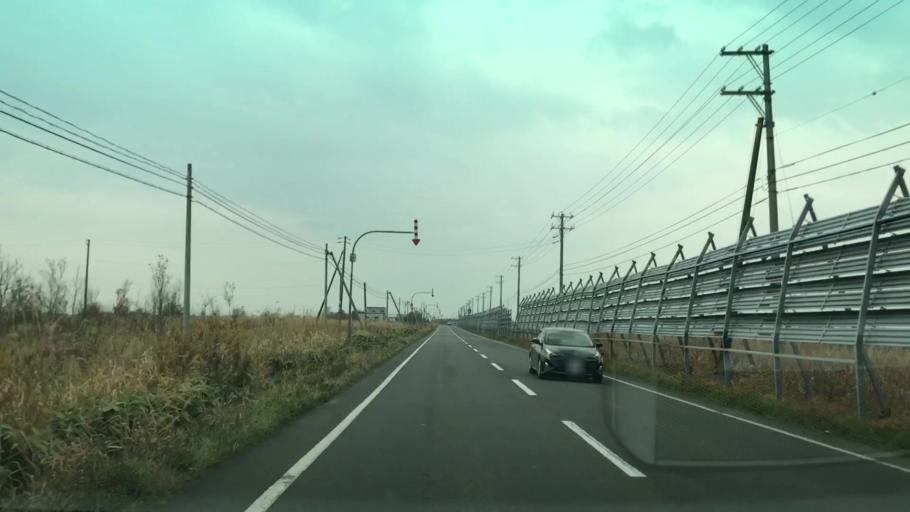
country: JP
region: Hokkaido
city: Ishikari
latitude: 43.2864
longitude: 141.4097
